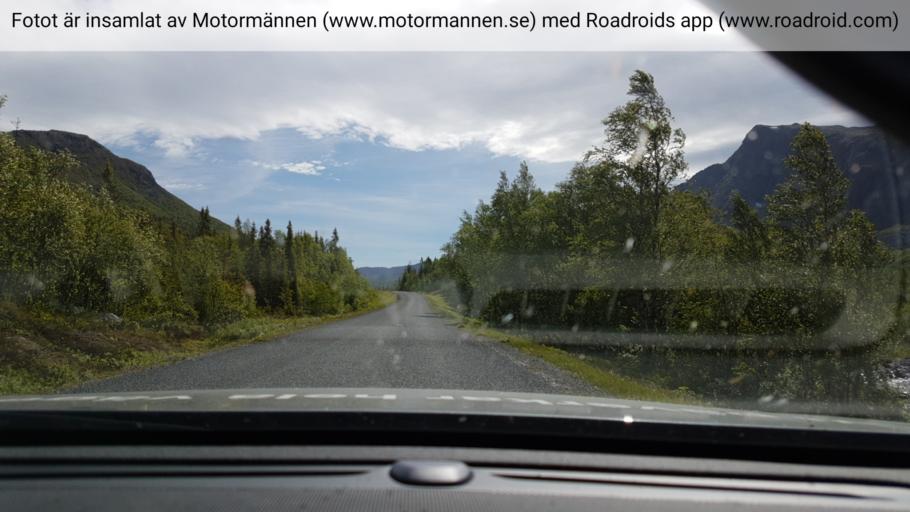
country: SE
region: Vaesterbotten
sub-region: Vilhelmina Kommun
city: Sjoberg
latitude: 65.2484
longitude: 15.4212
